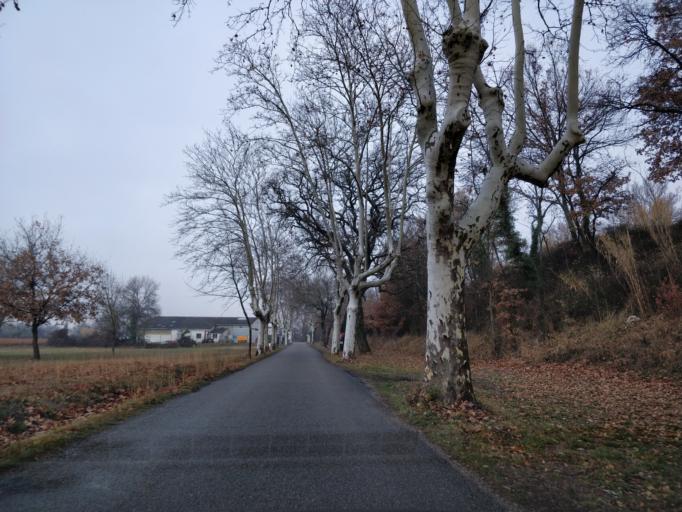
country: FR
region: Languedoc-Roussillon
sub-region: Departement du Gard
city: Saint-Mamert-du-Gard
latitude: 43.9007
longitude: 4.2113
